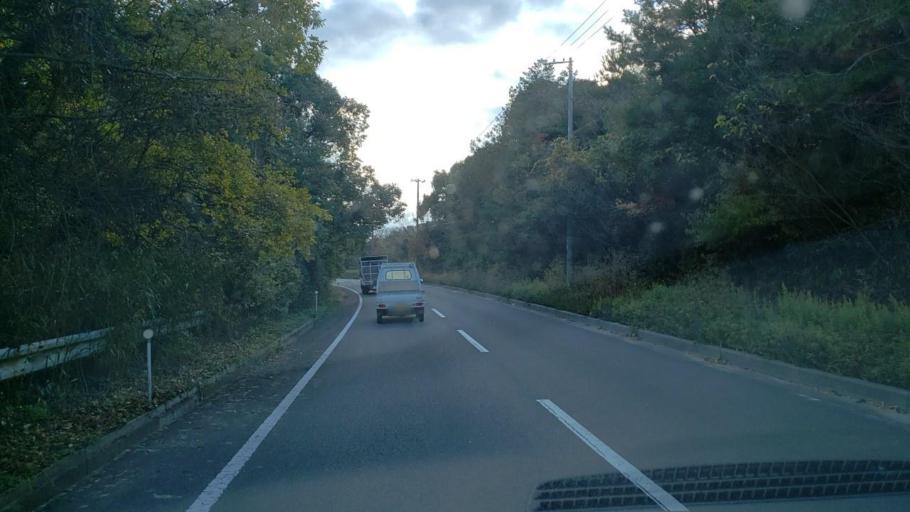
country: JP
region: Hyogo
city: Akashi
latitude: 34.5751
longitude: 134.9806
